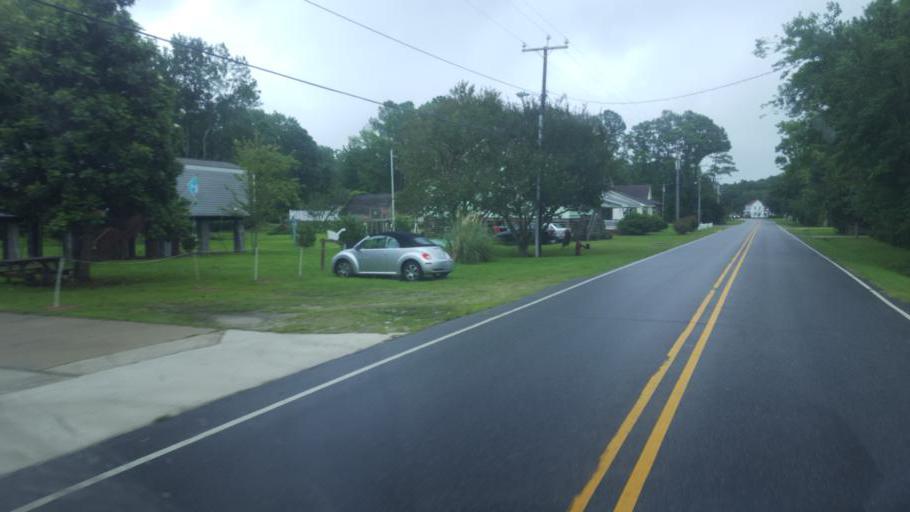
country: US
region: North Carolina
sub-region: Dare County
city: Wanchese
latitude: 35.8469
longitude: -75.6388
